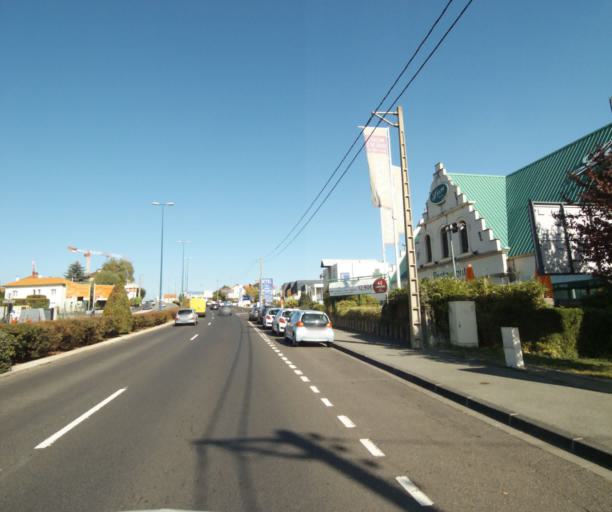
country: FR
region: Auvergne
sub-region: Departement du Puy-de-Dome
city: Aubiere
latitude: 45.7669
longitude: 3.1252
